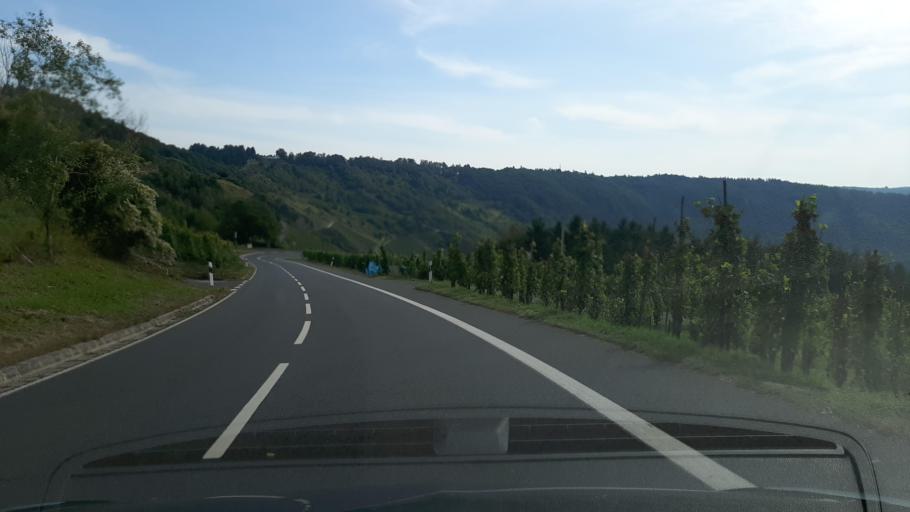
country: DE
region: Rheinland-Pfalz
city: Krov
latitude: 49.9869
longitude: 7.0932
